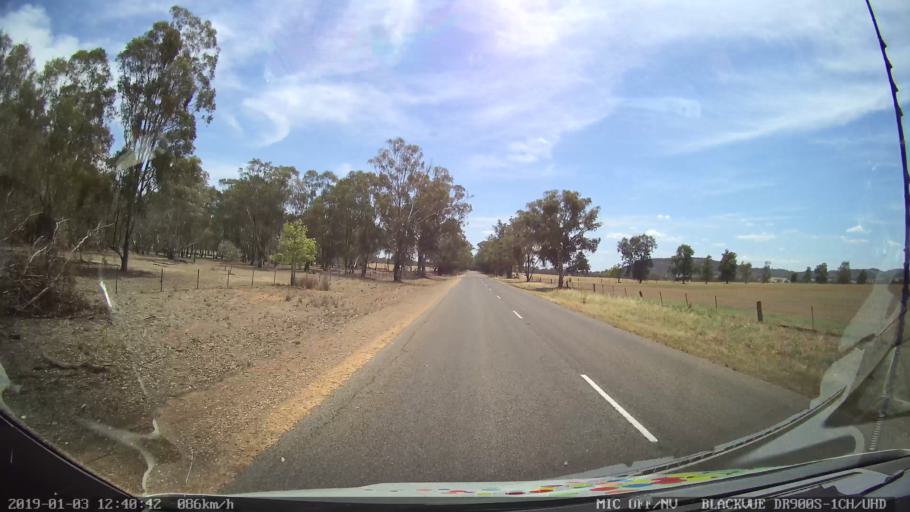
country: AU
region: New South Wales
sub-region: Weddin
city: Grenfell
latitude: -33.8093
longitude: 148.2134
